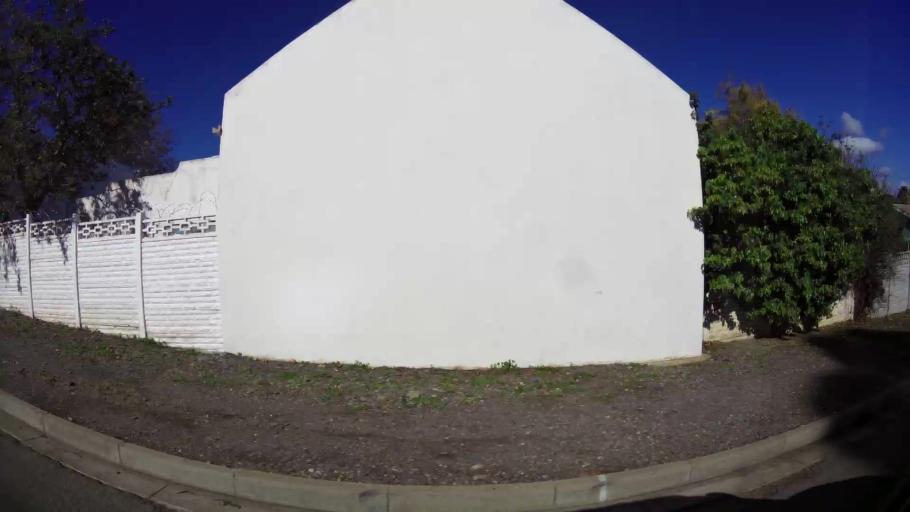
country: ZA
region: Western Cape
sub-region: Cape Winelands District Municipality
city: Ashton
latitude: -33.7961
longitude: 19.8915
